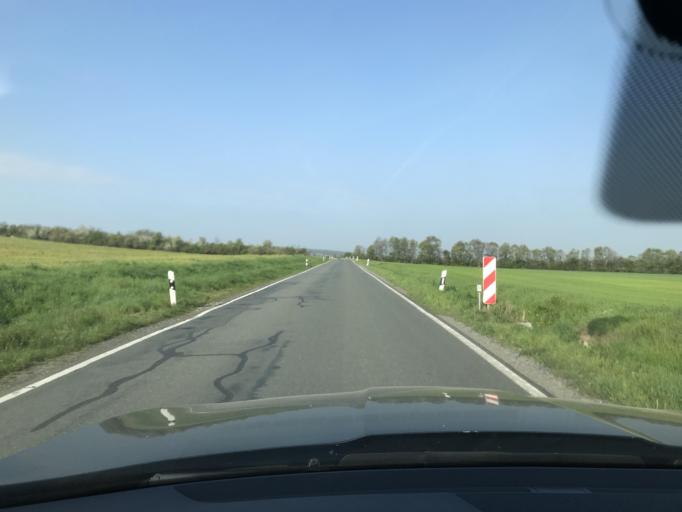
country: DE
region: Saxony-Anhalt
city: Halberstadt
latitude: 51.9804
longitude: 11.0286
